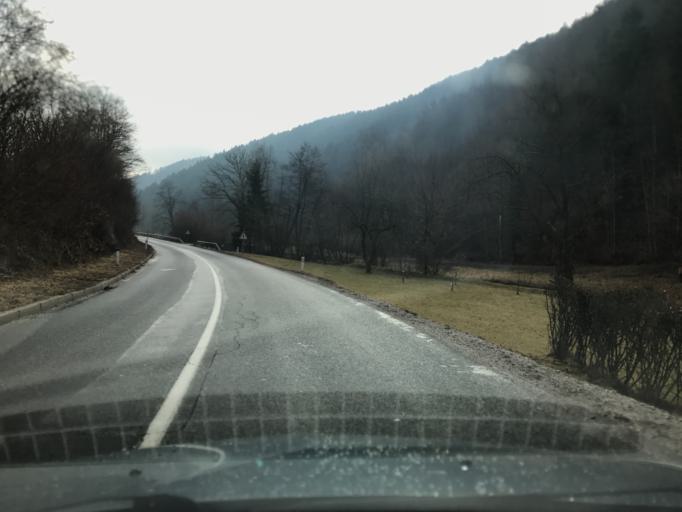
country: SI
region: Lukovica
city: Lukovica pri Domzalah
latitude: 46.2170
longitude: 14.7126
